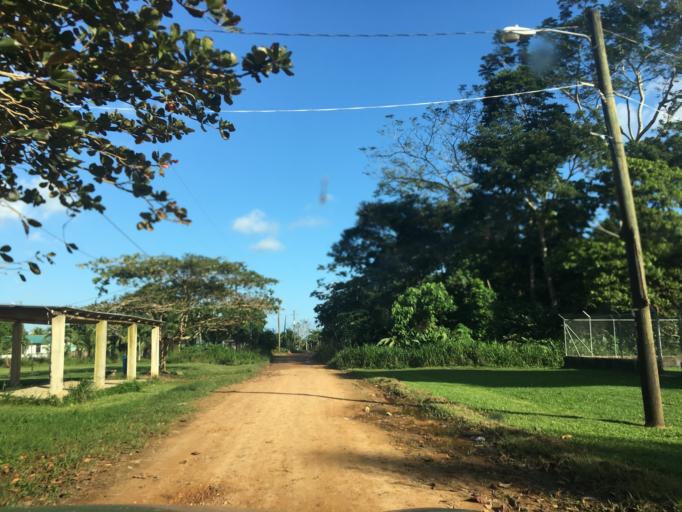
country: BZ
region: Stann Creek
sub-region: Dangriga
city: Dangriga
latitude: 16.7978
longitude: -88.3827
